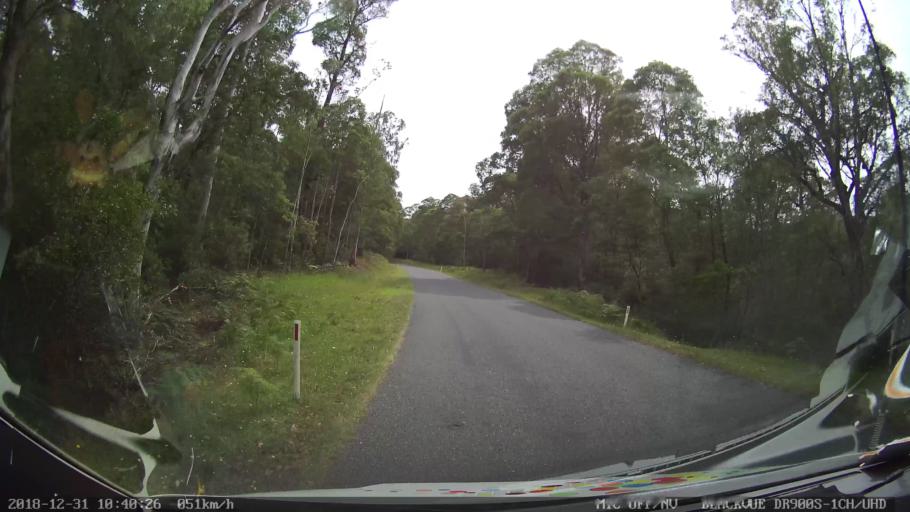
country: AU
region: New South Wales
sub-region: Snowy River
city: Jindabyne
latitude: -36.3915
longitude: 148.1815
